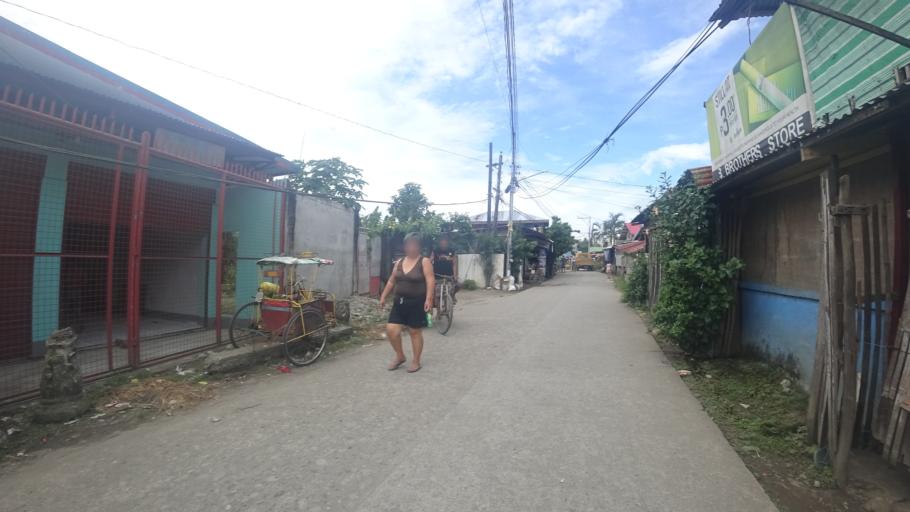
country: PH
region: Eastern Visayas
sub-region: Province of Leyte
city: Baras
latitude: 11.2086
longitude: 125.0140
